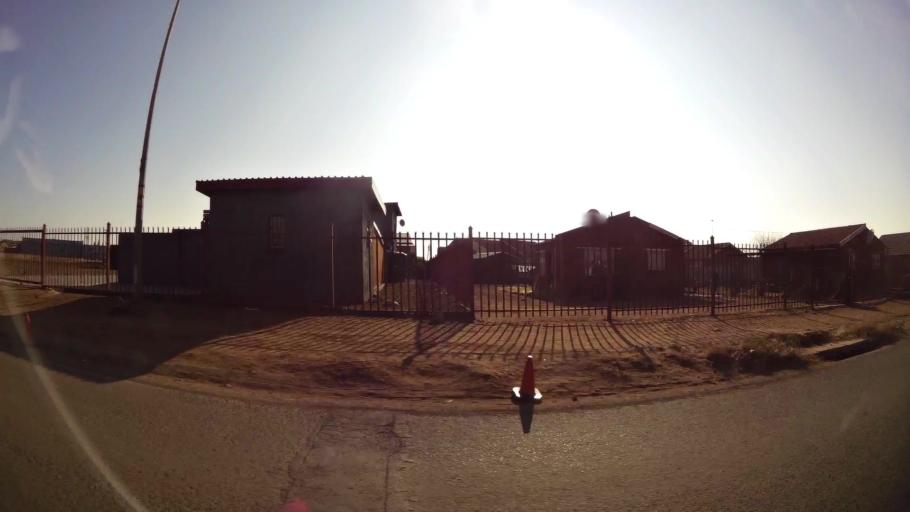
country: ZA
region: Orange Free State
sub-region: Mangaung Metropolitan Municipality
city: Bloemfontein
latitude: -29.2001
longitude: 26.2270
